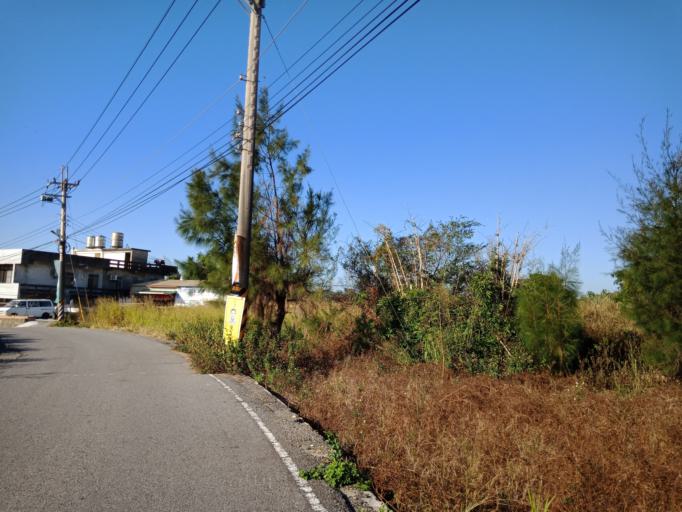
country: TW
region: Taiwan
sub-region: Miaoli
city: Miaoli
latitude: 24.4924
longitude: 120.6949
